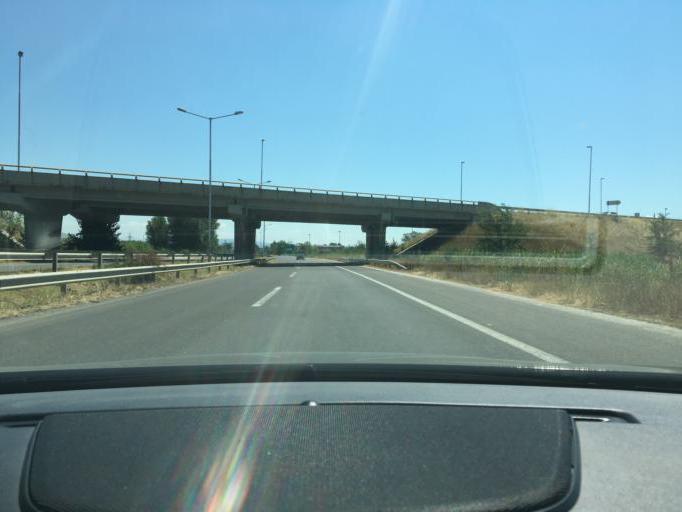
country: MK
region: Ilinden
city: Jurumleri
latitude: 41.9947
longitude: 21.5326
